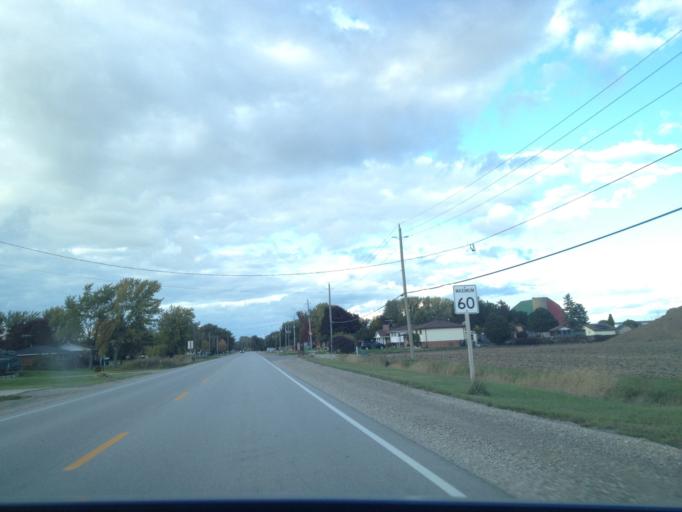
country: US
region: Michigan
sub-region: Wayne County
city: Grosse Pointe Farms
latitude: 42.2554
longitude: -82.7138
